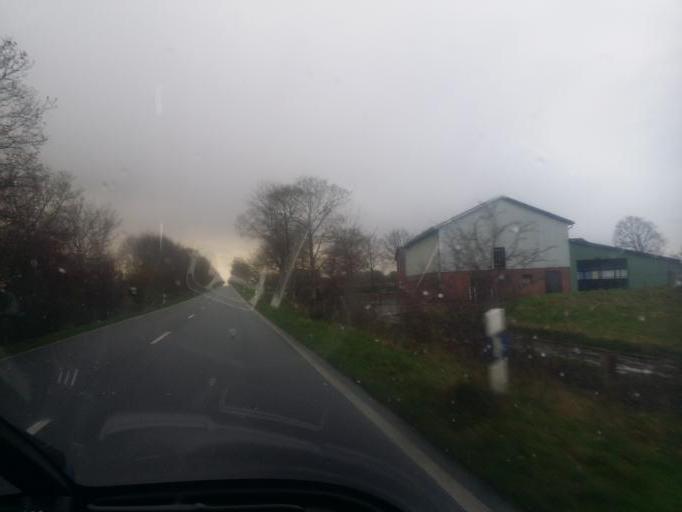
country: DE
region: Schleswig-Holstein
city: Immenstedt
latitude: 54.1744
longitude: 9.3137
